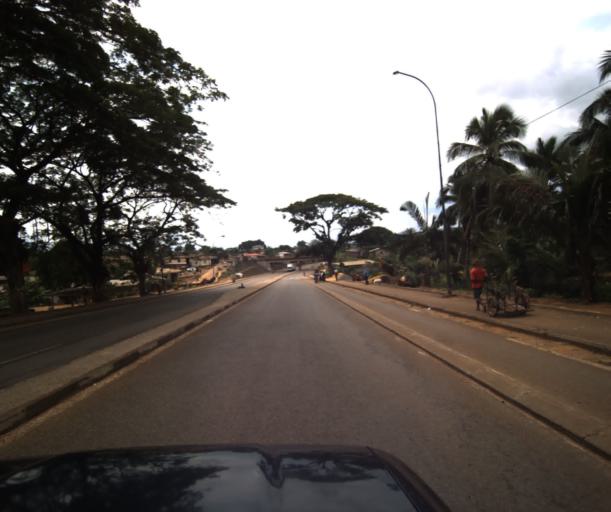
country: CM
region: Littoral
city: Edea
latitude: 3.7927
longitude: 10.1339
